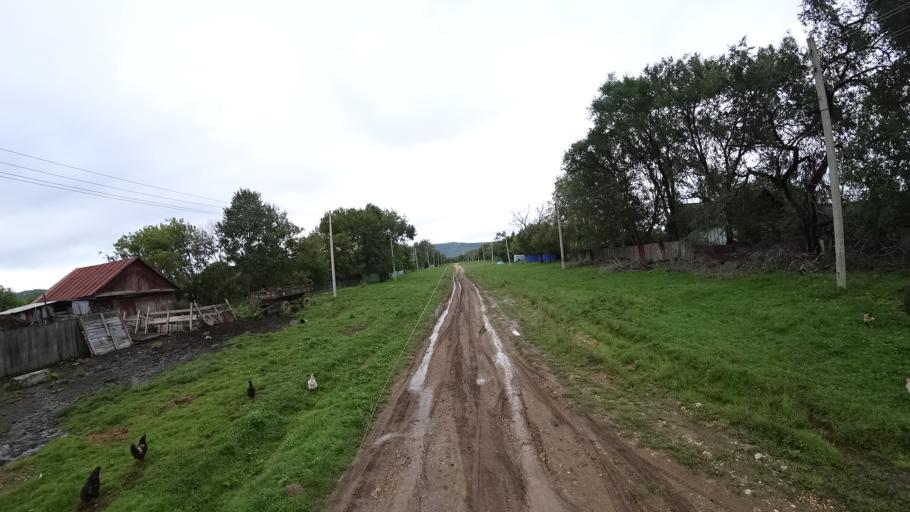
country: RU
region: Primorskiy
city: Rettikhovka
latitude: 44.1370
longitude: 132.6526
